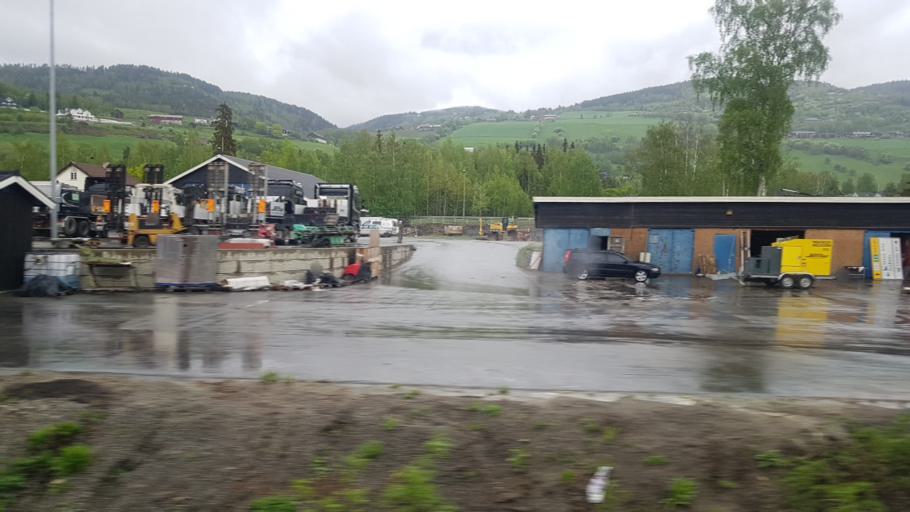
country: NO
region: Oppland
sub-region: Nord-Fron
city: Vinstra
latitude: 61.5821
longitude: 9.7604
